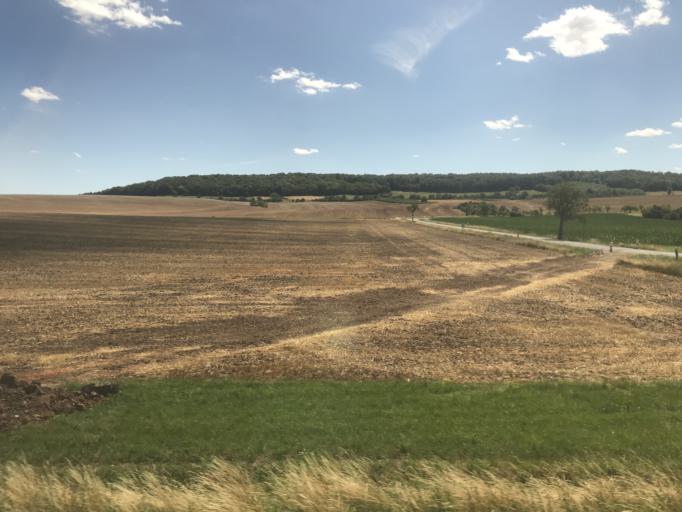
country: FR
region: Lorraine
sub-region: Departement de la Moselle
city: Crehange
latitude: 48.9679
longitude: 6.5157
